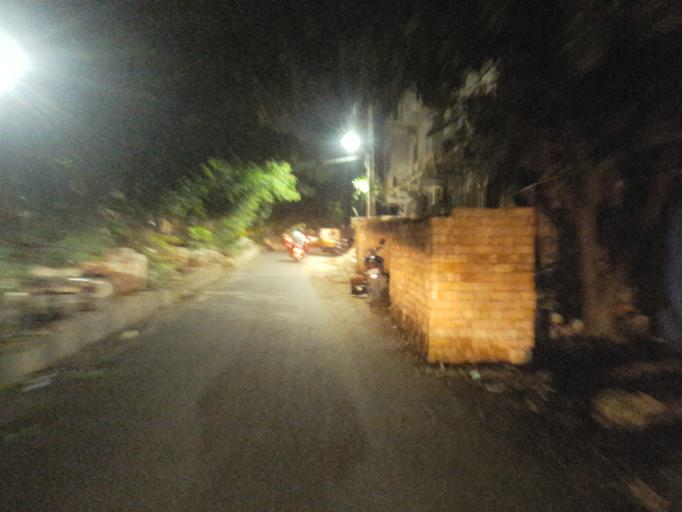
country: IN
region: Telangana
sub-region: Rangareddi
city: Kukatpalli
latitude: 17.4798
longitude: 78.3928
